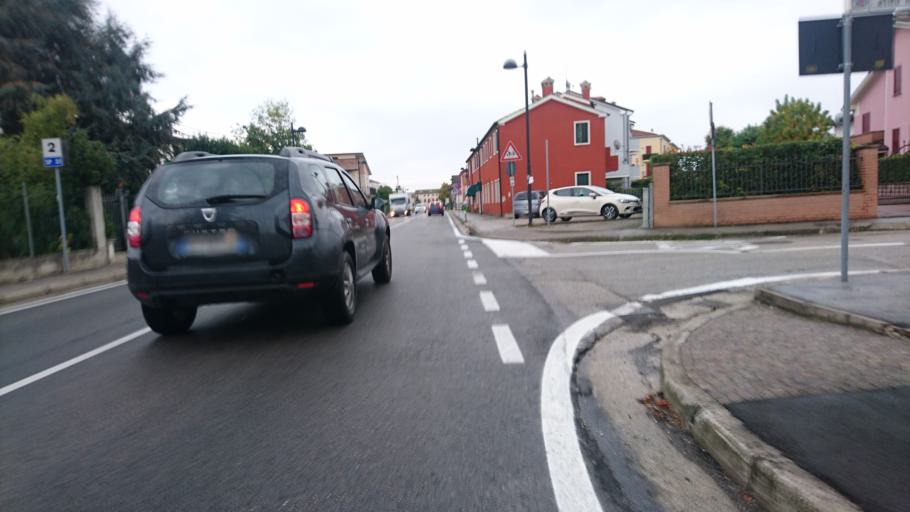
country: IT
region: Veneto
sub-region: Provincia di Padova
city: Veggiano
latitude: 45.4484
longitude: 11.7114
